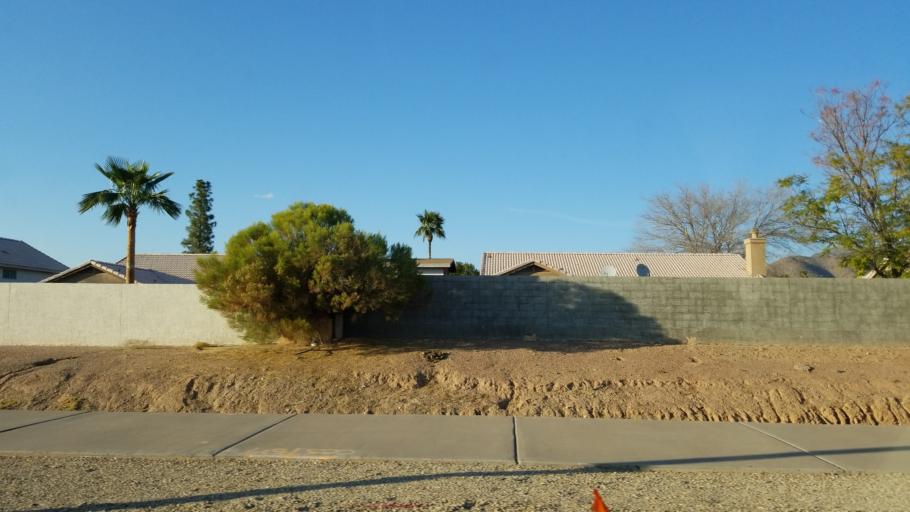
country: US
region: Arizona
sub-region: Maricopa County
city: Scottsdale
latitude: 33.5826
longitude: -111.8443
